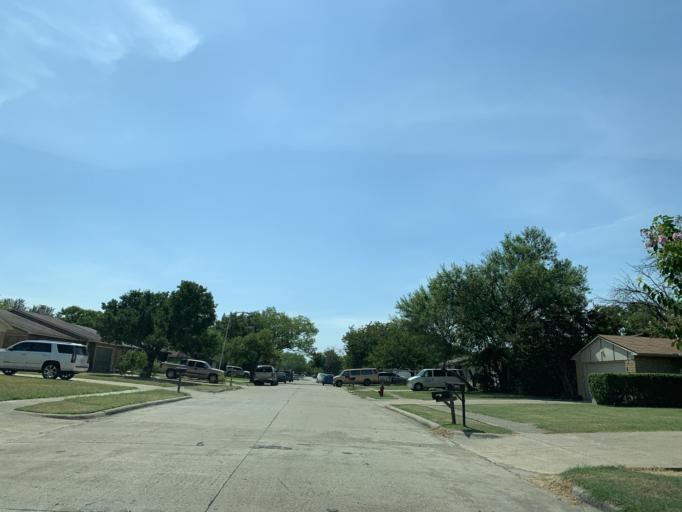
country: US
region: Texas
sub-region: Dallas County
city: Cedar Hill
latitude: 32.6523
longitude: -97.0187
